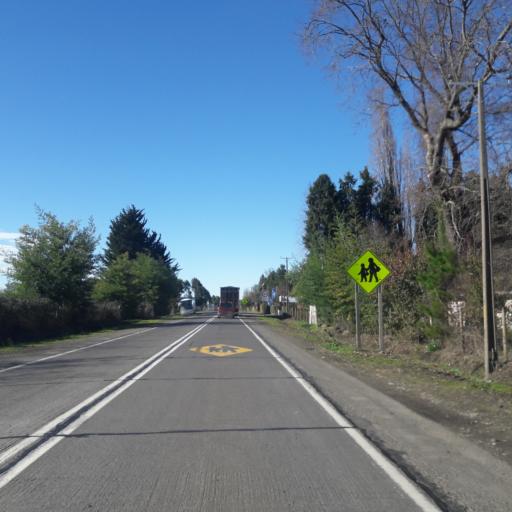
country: CL
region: Araucania
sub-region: Provincia de Malleco
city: Angol
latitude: -37.7733
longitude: -72.5474
